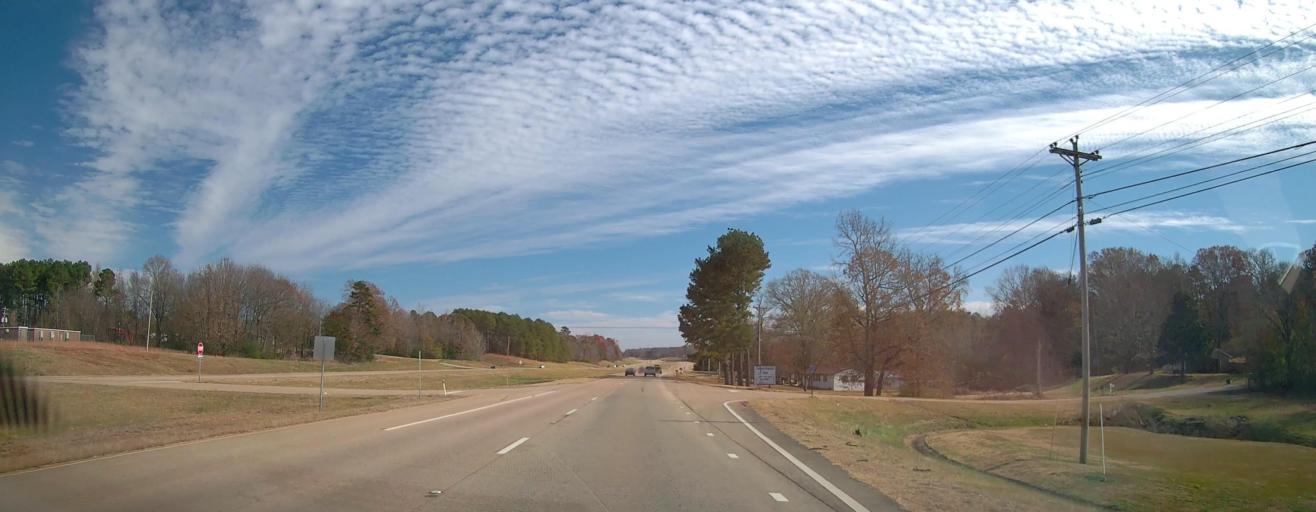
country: US
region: Mississippi
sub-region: Tippah County
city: Ripley
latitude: 34.9530
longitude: -88.8365
